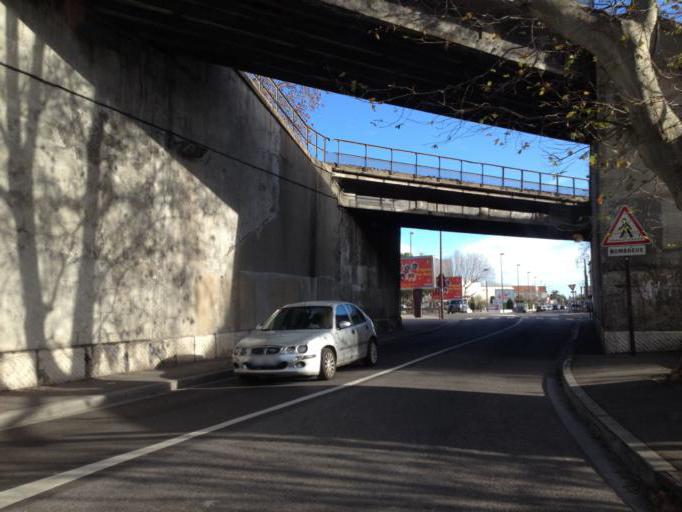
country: FR
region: Provence-Alpes-Cote d'Azur
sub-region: Departement du Vaucluse
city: Avignon
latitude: 43.9423
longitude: 4.8213
